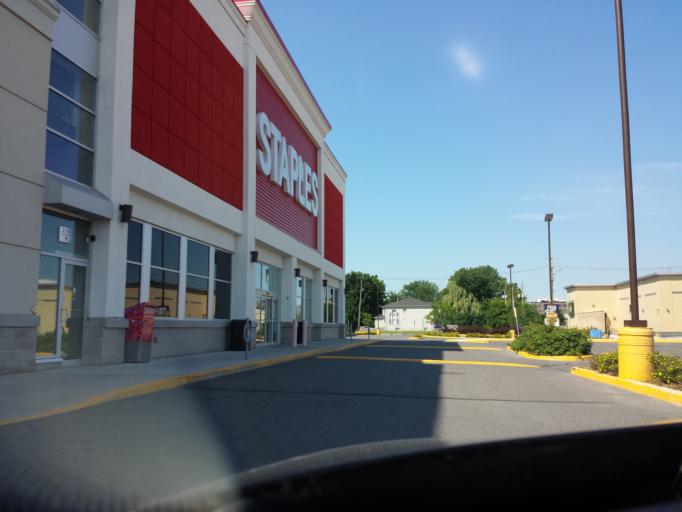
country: CA
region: Ontario
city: Ottawa
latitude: 45.3698
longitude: -75.7686
